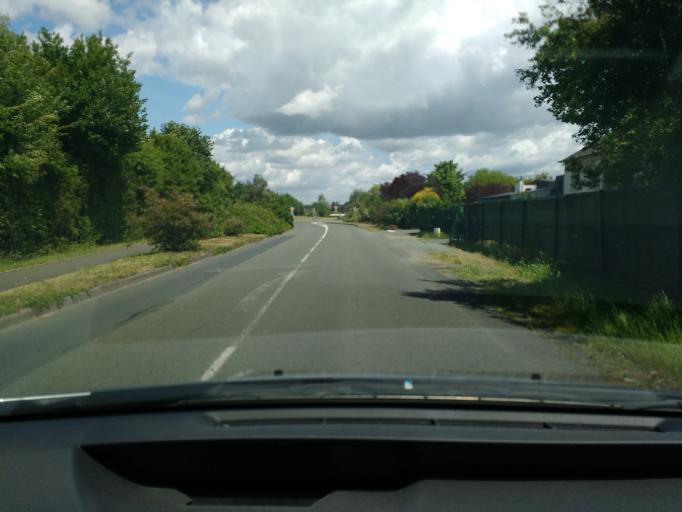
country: FR
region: Pays de la Loire
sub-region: Departement de Maine-et-Loire
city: Trelaze
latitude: 47.4801
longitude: -0.4891
